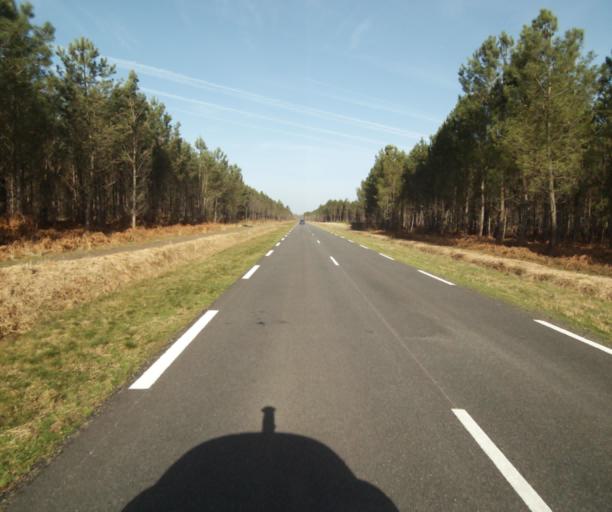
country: FR
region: Aquitaine
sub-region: Departement de la Gironde
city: Grignols
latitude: 44.1869
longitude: -0.1027
